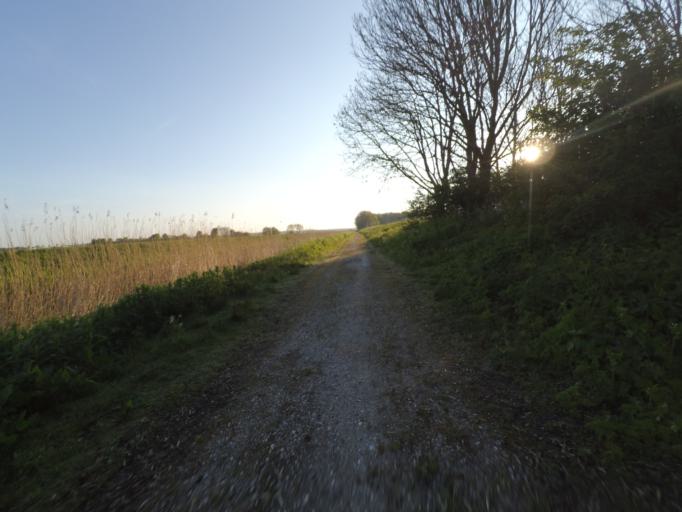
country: NL
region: Flevoland
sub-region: Gemeente Lelystad
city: Lelystad
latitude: 52.4535
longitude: 5.4994
